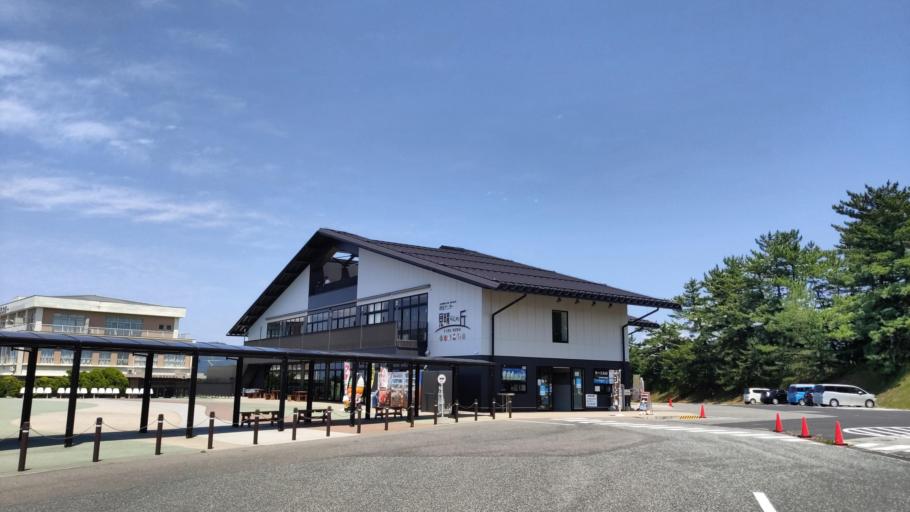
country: JP
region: Tottori
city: Tottori
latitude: 35.5413
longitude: 134.2382
